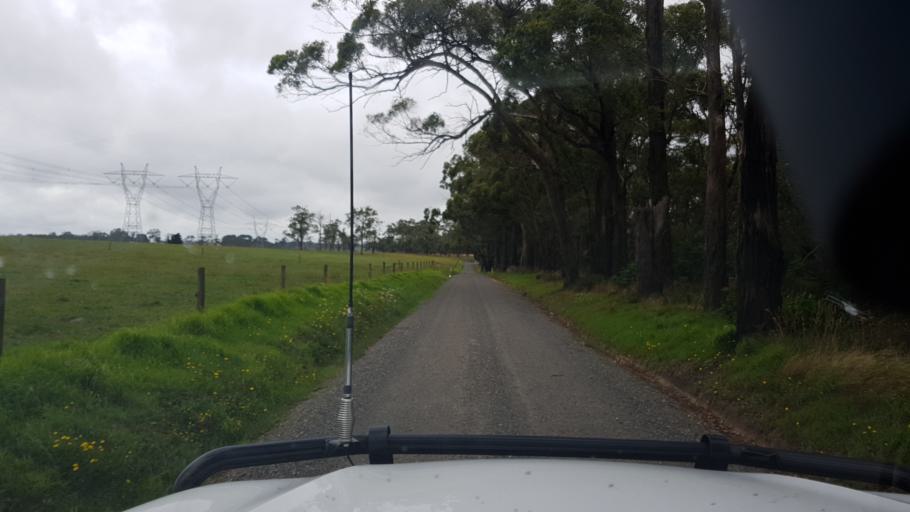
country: AU
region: Victoria
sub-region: Baw Baw
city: Warragul
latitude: -38.1898
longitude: 145.8487
